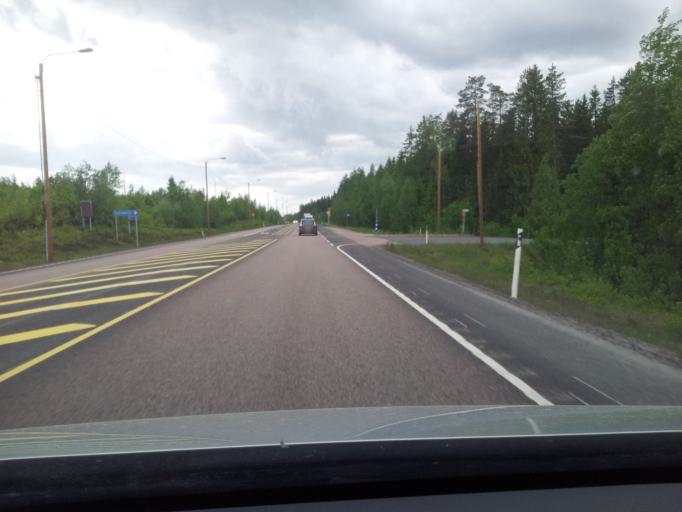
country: FI
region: South Karelia
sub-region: Lappeenranta
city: Taavetti
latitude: 60.9131
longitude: 27.3509
